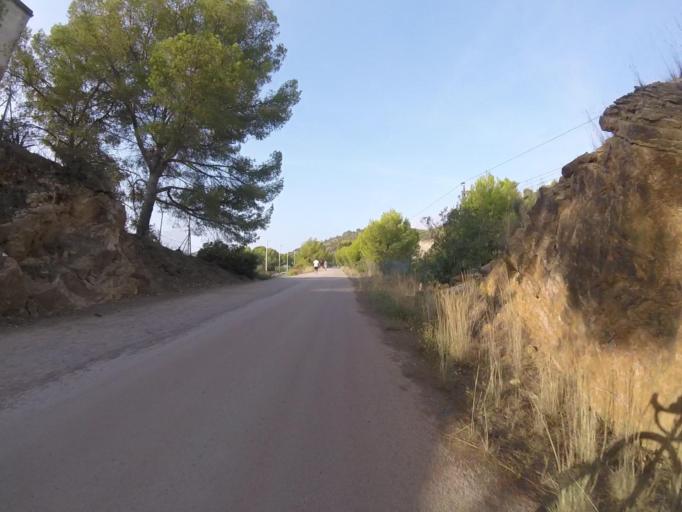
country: ES
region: Valencia
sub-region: Provincia de Castello
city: Orpesa/Oropesa del Mar
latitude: 40.0806
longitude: 0.1352
